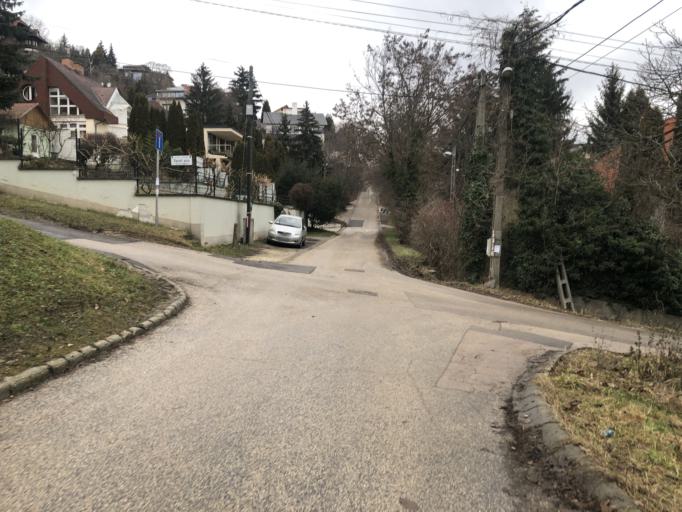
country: HU
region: Pest
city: Budakeszi
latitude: 47.5476
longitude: 18.9466
